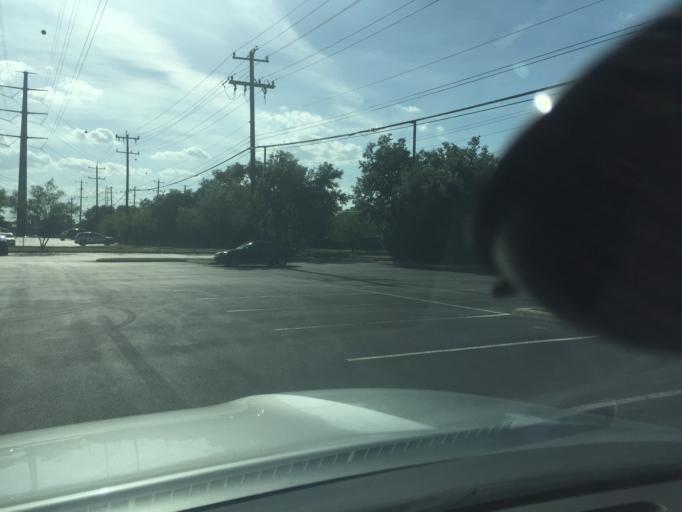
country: US
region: Texas
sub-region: Bexar County
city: Hollywood Park
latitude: 29.6175
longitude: -98.4904
